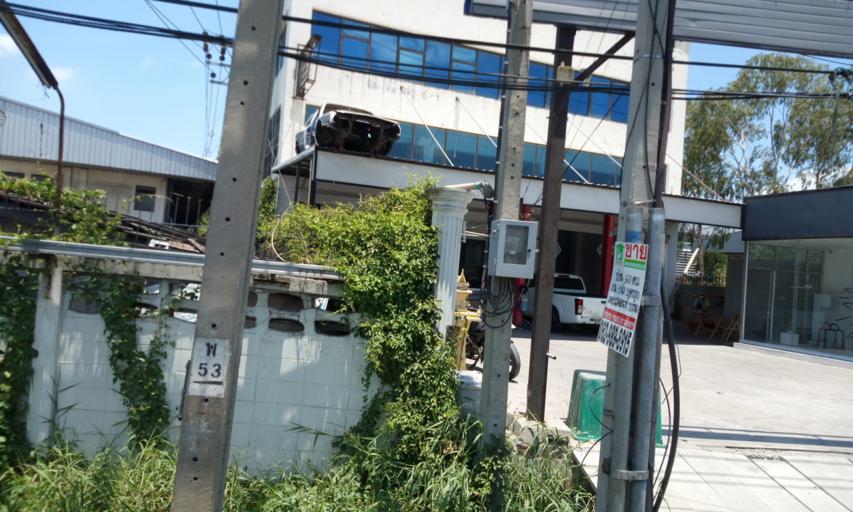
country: TH
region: Bangkok
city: Bang Na
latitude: 13.6248
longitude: 100.7062
